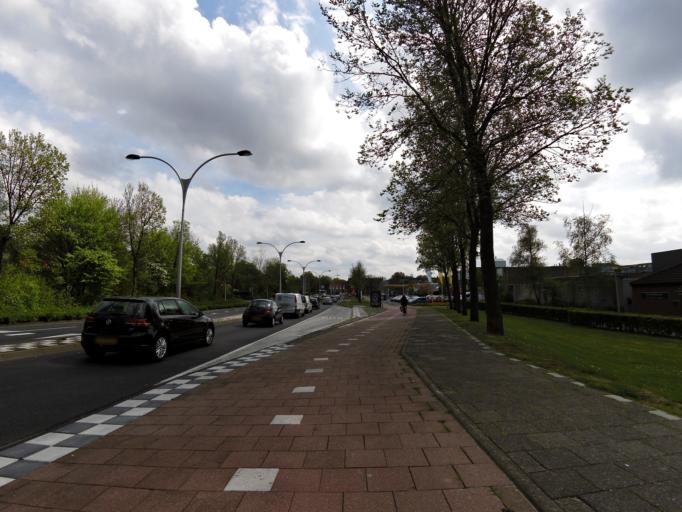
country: NL
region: South Holland
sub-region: Gemeente Hellevoetsluis
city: Hellevoetsluis
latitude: 51.8334
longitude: 4.1489
